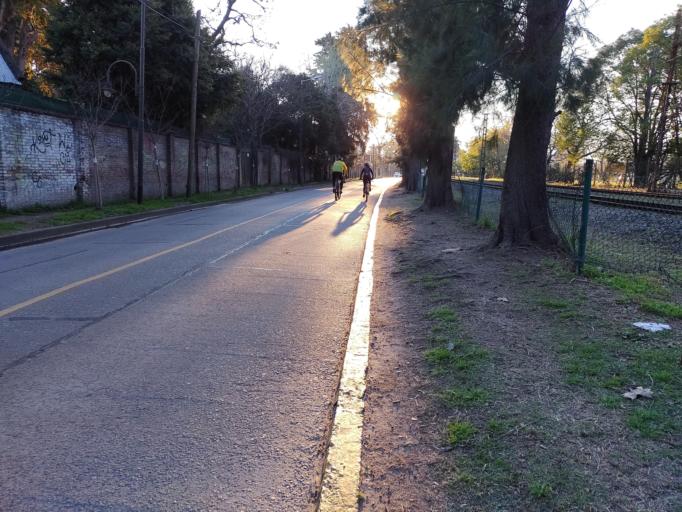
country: AR
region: Buenos Aires
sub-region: Partido de San Isidro
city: San Isidro
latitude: -34.4474
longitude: -58.5296
